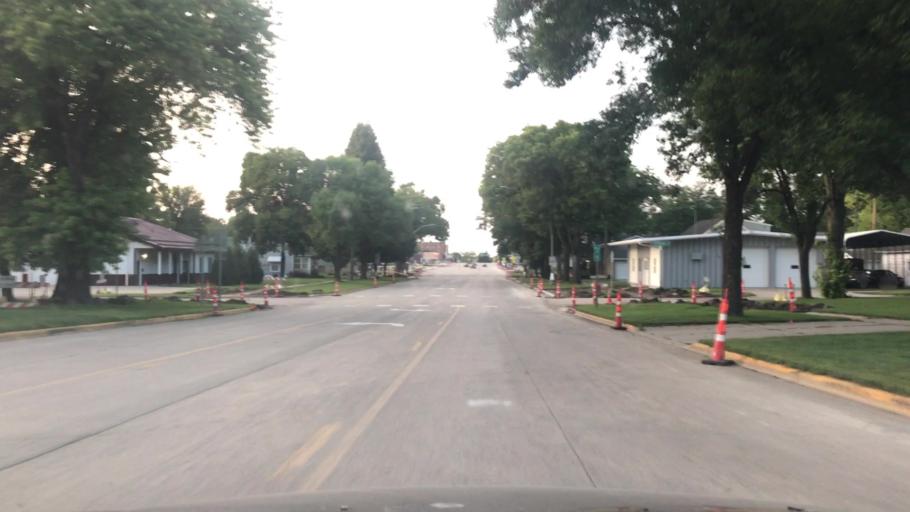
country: US
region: Minnesota
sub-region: Redwood County
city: Redwood Falls
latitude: 44.5356
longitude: -95.1195
